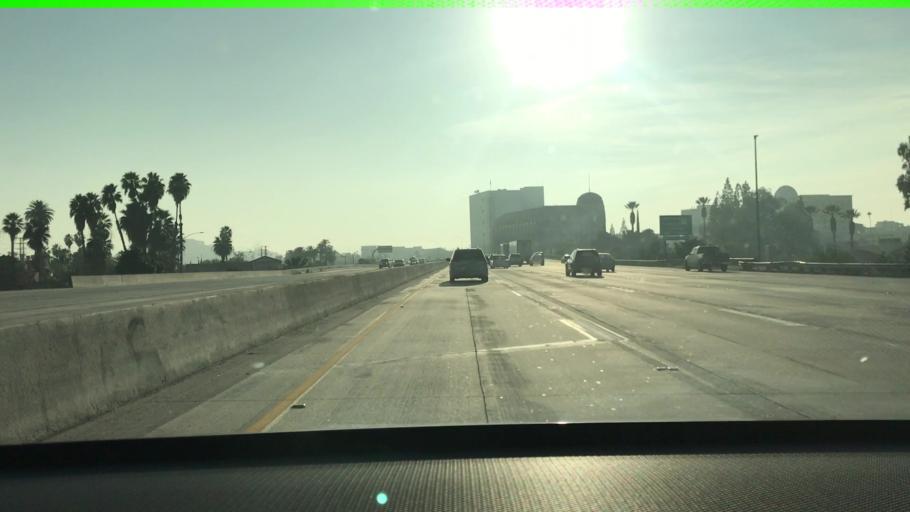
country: US
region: California
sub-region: Riverside County
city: Rubidoux
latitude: 33.9821
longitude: -117.3677
